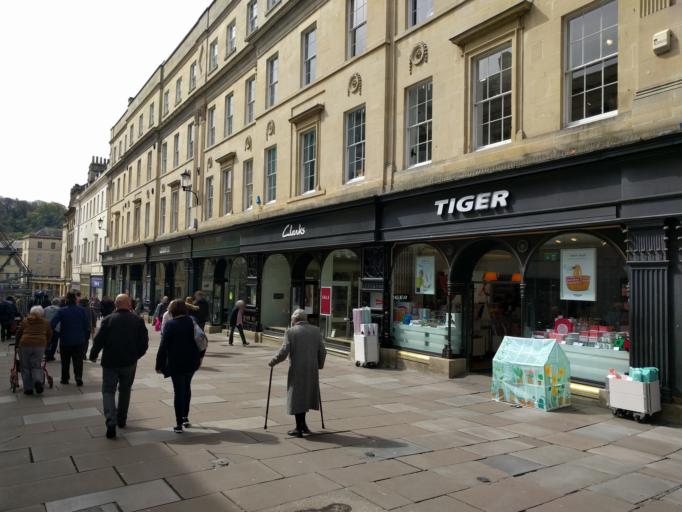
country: GB
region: England
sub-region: Bath and North East Somerset
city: Bath
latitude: 51.3824
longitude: -2.3605
